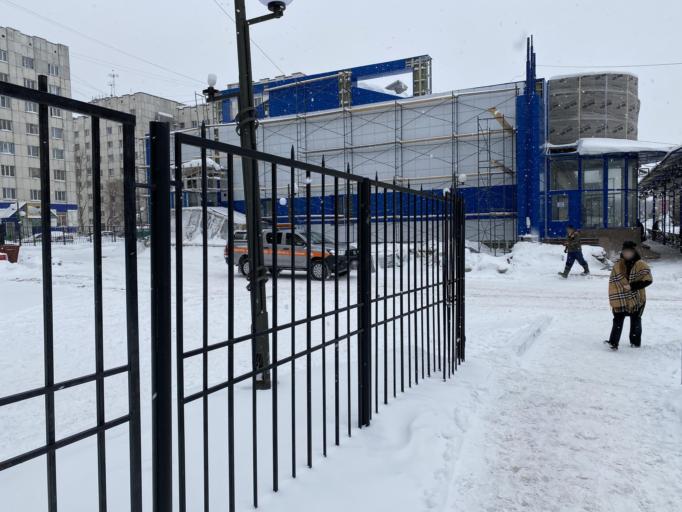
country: RU
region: Tjumen
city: Tobol'sk
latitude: 58.2274
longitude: 68.2694
